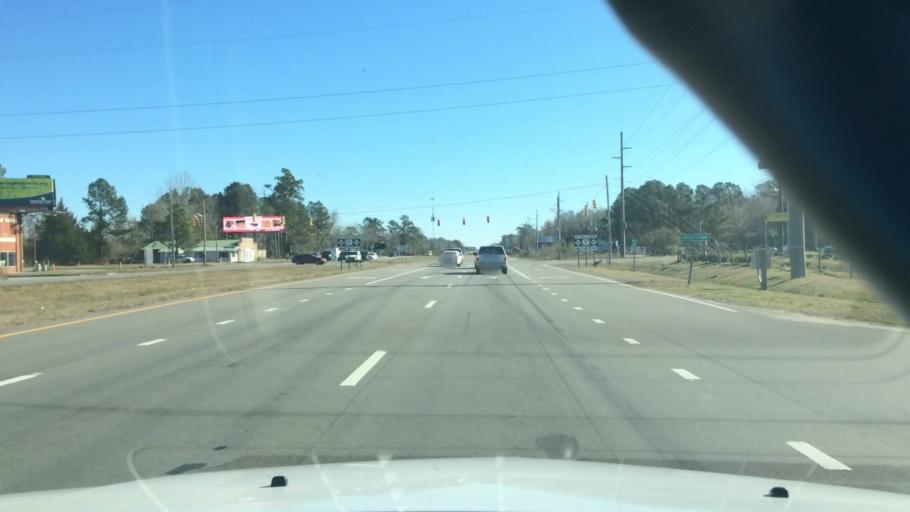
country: US
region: North Carolina
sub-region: Brunswick County
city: Sunset Beach
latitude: 33.9462
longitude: -78.5034
